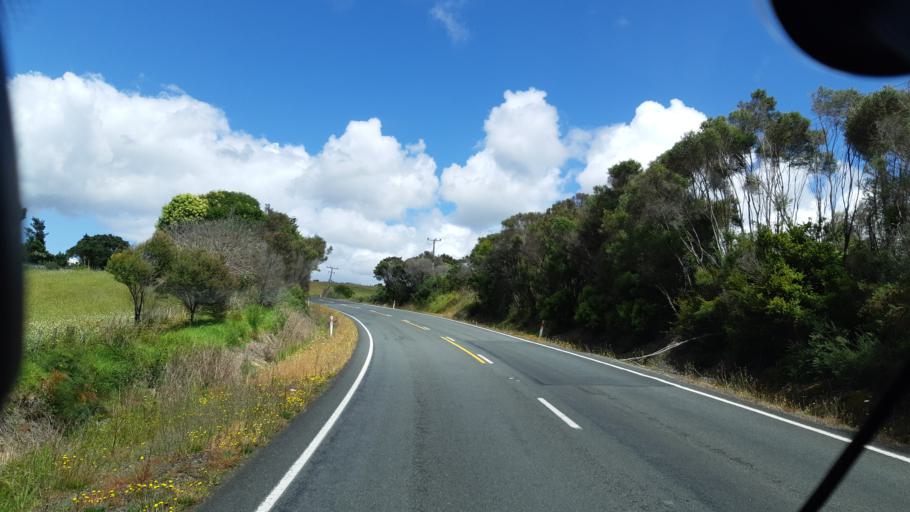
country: NZ
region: Northland
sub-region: Far North District
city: Waimate North
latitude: -35.2942
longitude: 173.6179
